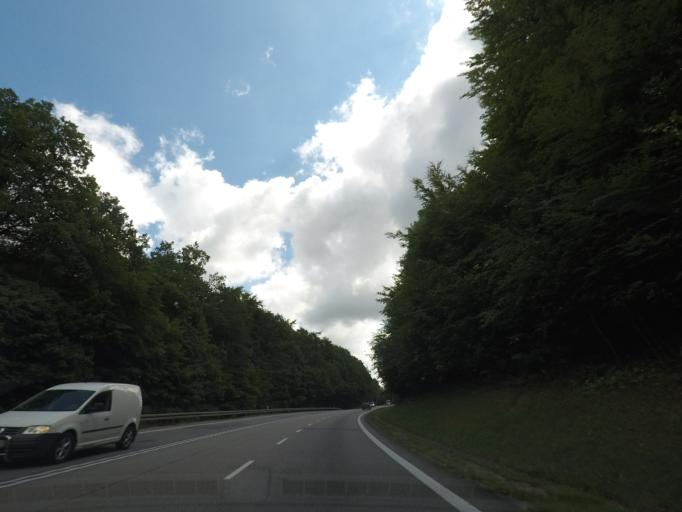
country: PL
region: Pomeranian Voivodeship
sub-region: Powiat wejherowski
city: Luzino
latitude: 54.5814
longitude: 18.0869
